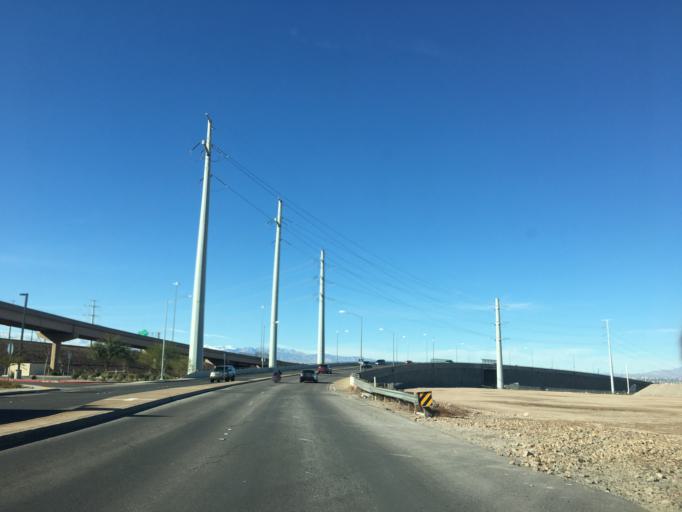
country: US
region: Nevada
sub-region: Clark County
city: Henderson
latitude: 36.0372
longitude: -115.0160
